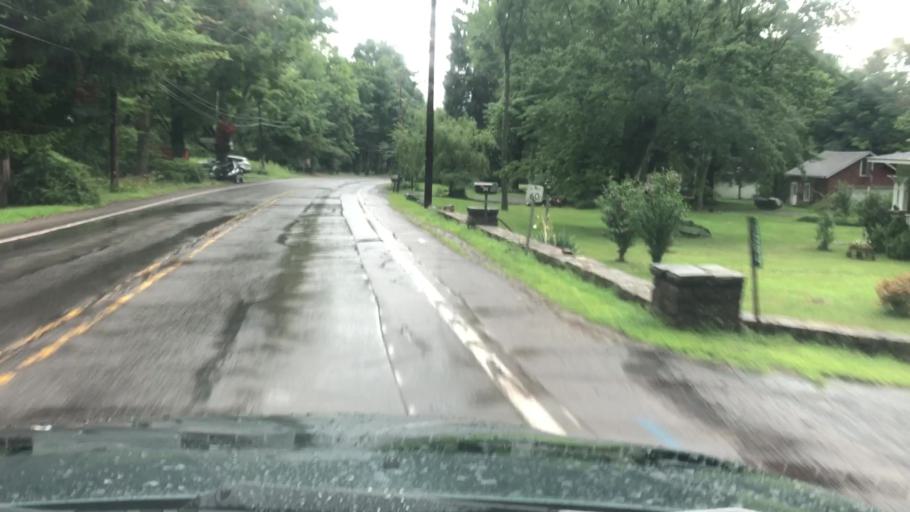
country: US
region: Pennsylvania
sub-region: Monroe County
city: Mountainhome
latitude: 41.1839
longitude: -75.2650
